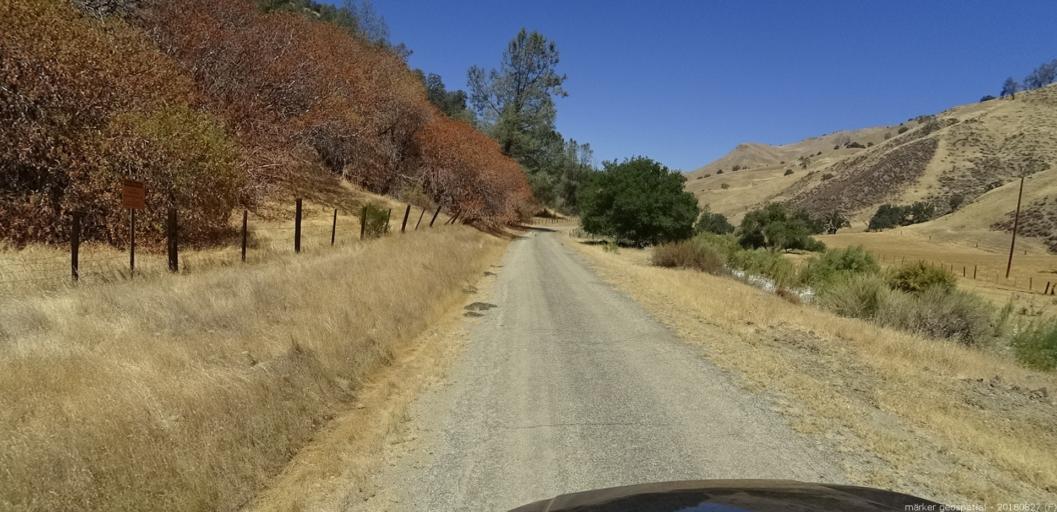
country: US
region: California
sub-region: Monterey County
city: King City
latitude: 36.2769
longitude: -120.8423
